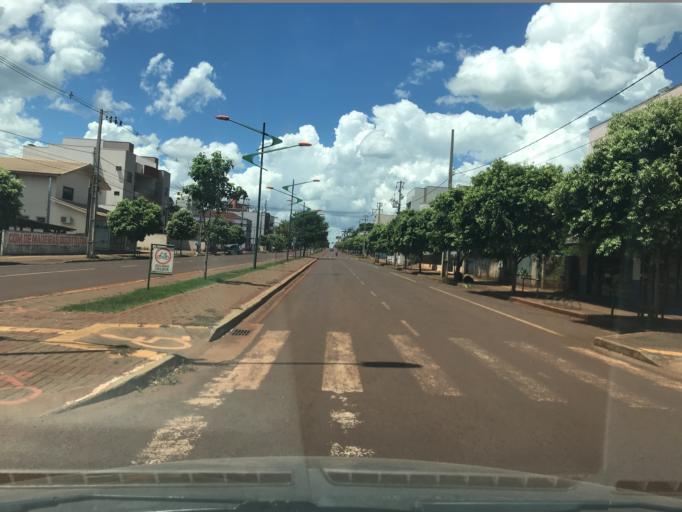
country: BR
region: Parana
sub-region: Palotina
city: Palotina
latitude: -24.2847
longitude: -53.8458
